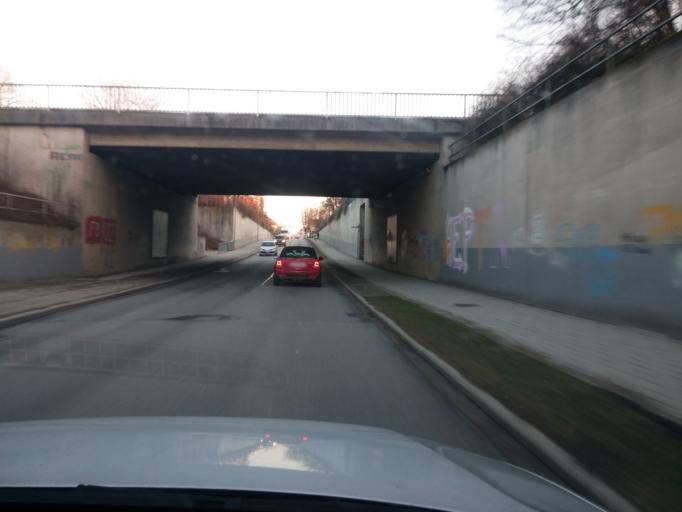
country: DE
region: Bavaria
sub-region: Upper Bavaria
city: Feldkirchen
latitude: 48.1509
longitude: 11.7268
